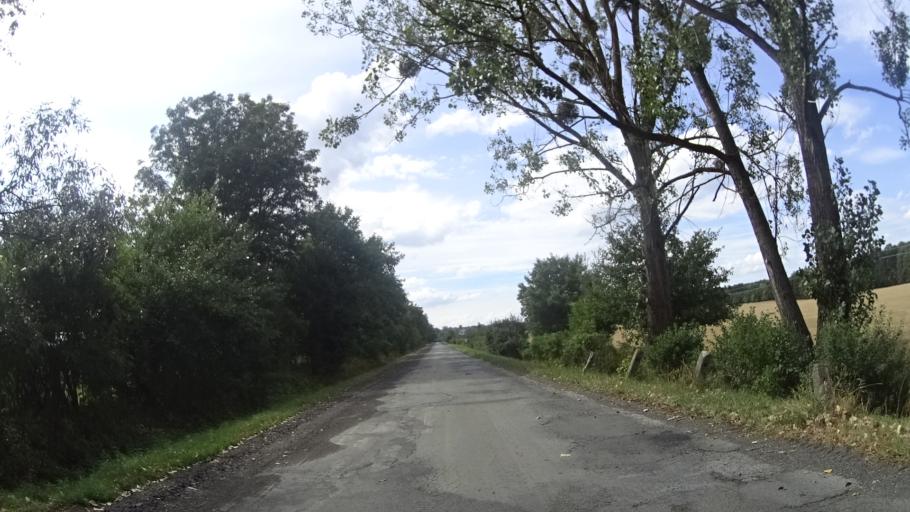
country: CZ
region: Olomoucky
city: Cervenka
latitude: 49.7164
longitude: 17.0470
